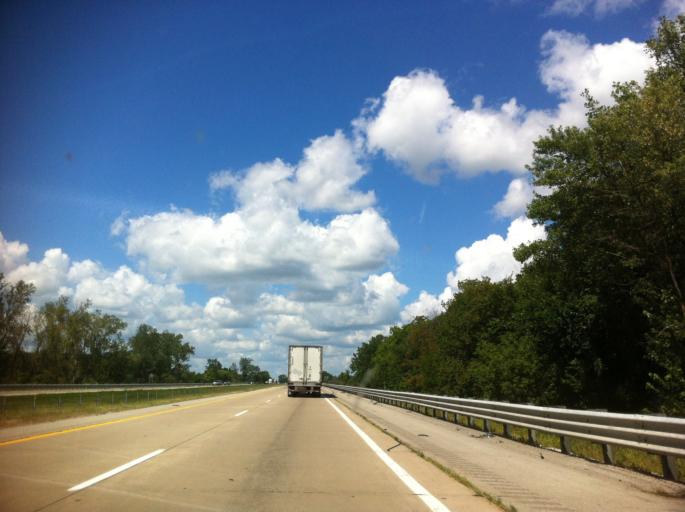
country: US
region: Michigan
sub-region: Monroe County
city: Dundee
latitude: 41.9836
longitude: -83.6783
